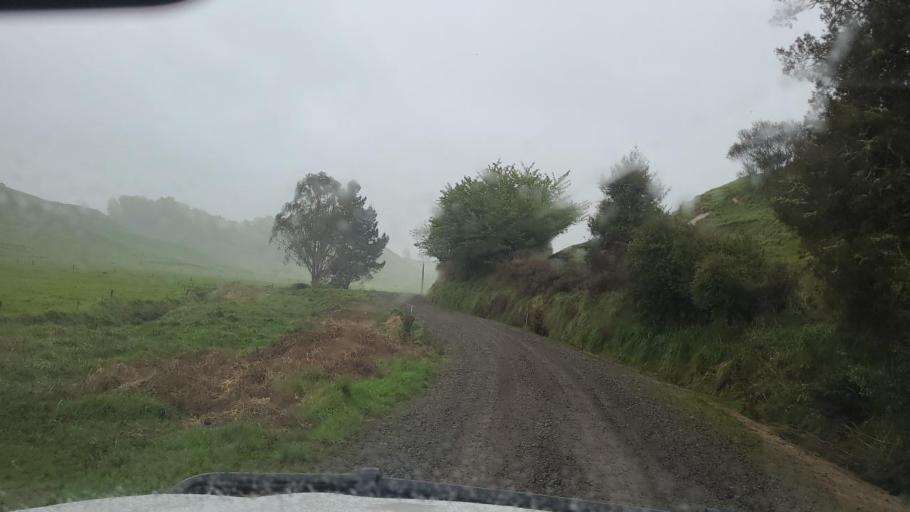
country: NZ
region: Taranaki
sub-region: South Taranaki District
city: Eltham
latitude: -39.2520
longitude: 174.5335
